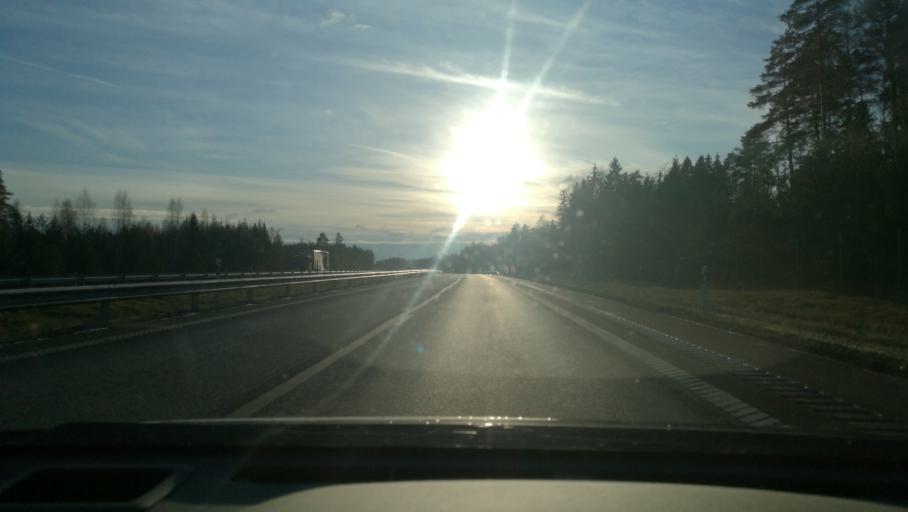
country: SE
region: Vaestmanland
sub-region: Kopings Kommun
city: Koping
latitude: 59.4935
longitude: 15.9216
